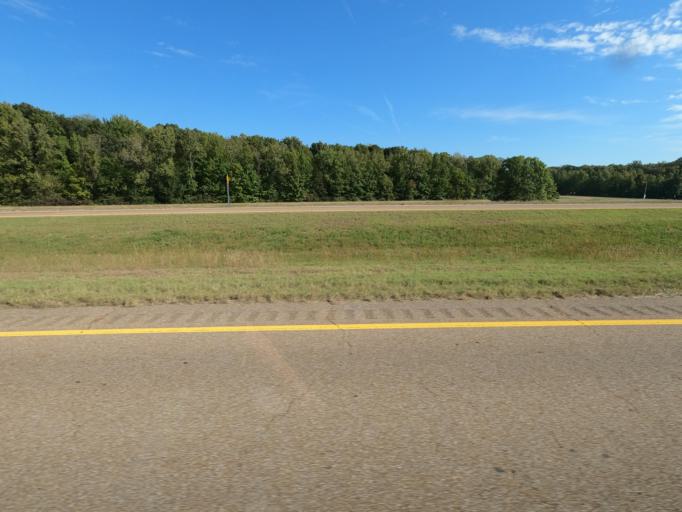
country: US
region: Tennessee
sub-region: Shelby County
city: Millington
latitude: 35.3201
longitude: -89.8752
